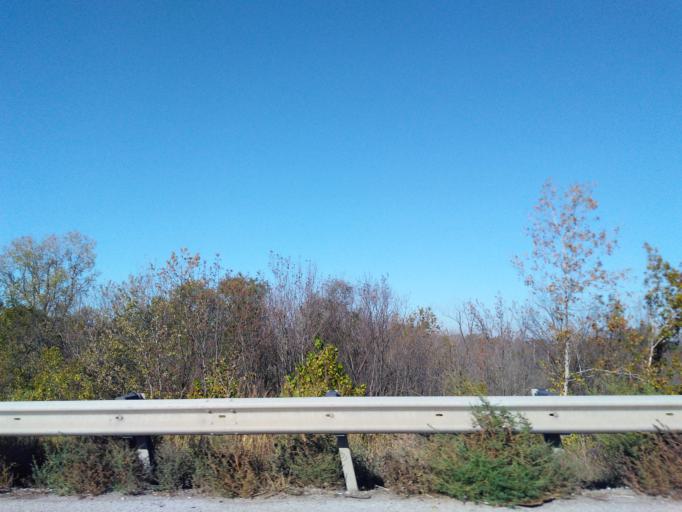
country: US
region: Illinois
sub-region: Saint Clair County
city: Washington Park
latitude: 38.6073
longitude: -90.0832
